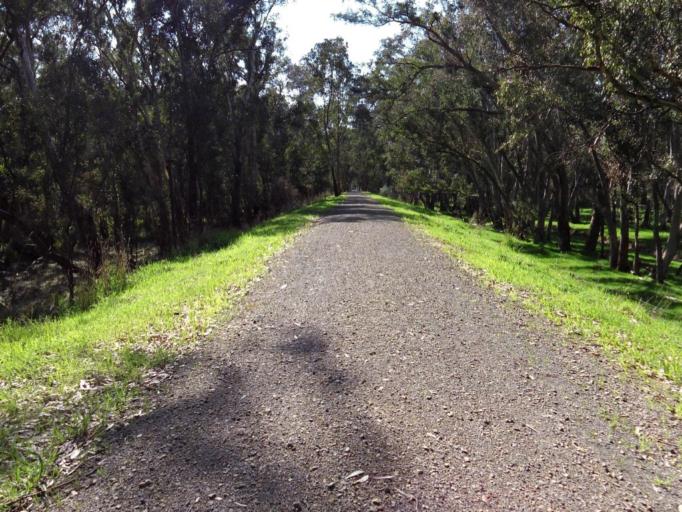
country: AU
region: Victoria
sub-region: Murrindindi
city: Alexandra
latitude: -37.1610
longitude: 145.5624
